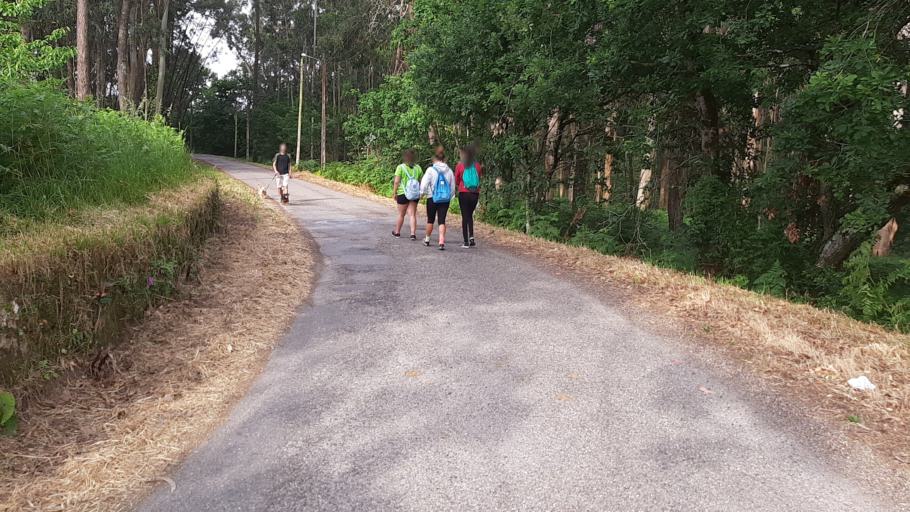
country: ES
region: Galicia
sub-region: Provincia de Pontevedra
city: O Rosal
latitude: 41.9296
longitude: -8.8433
